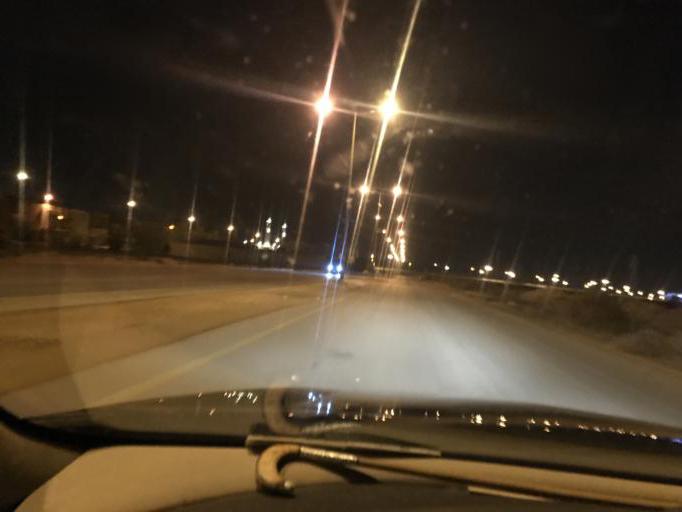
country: SA
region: Ar Riyad
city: Riyadh
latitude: 24.8184
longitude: 46.7216
